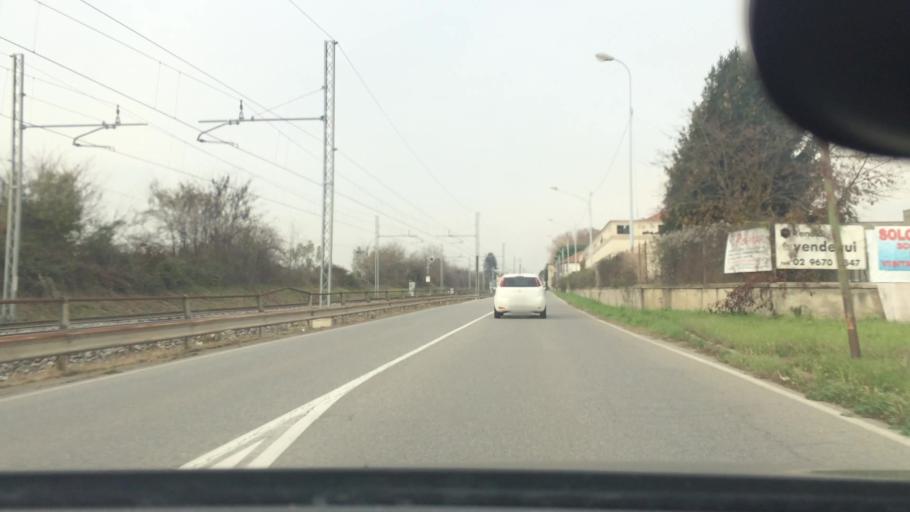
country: IT
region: Lombardy
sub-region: Provincia di Como
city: Rovello Porro
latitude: 45.6618
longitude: 9.0382
